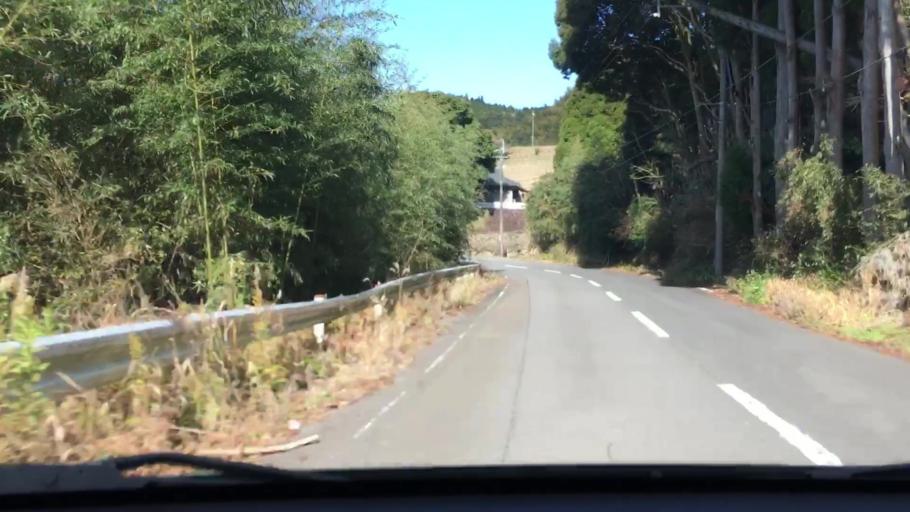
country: JP
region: Kagoshima
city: Ijuin
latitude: 31.7301
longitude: 130.4194
